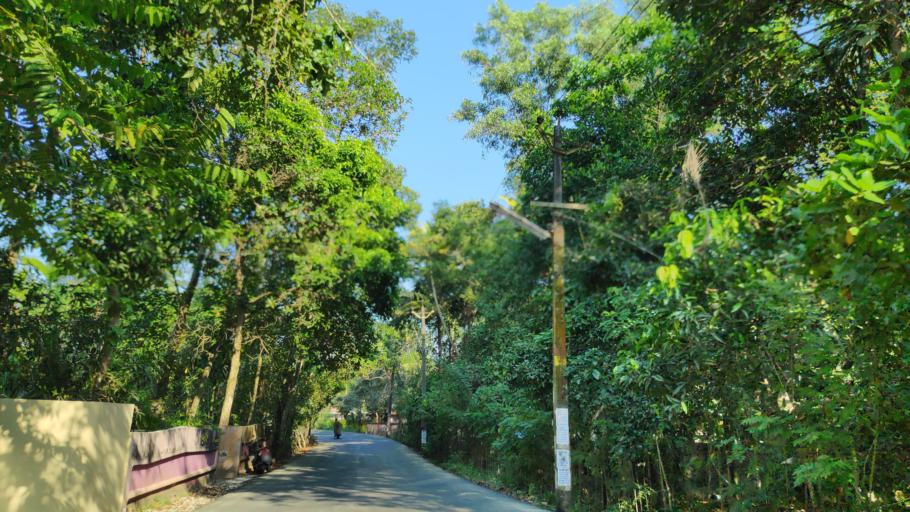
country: IN
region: Kerala
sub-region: Alappuzha
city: Alleppey
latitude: 9.5682
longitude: 76.3120
